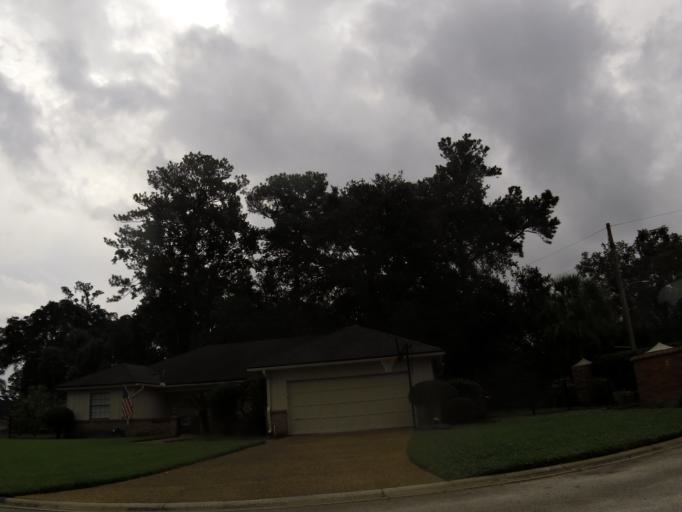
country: US
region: Florida
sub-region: Clay County
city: Bellair-Meadowbrook Terrace
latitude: 30.2511
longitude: -81.7041
